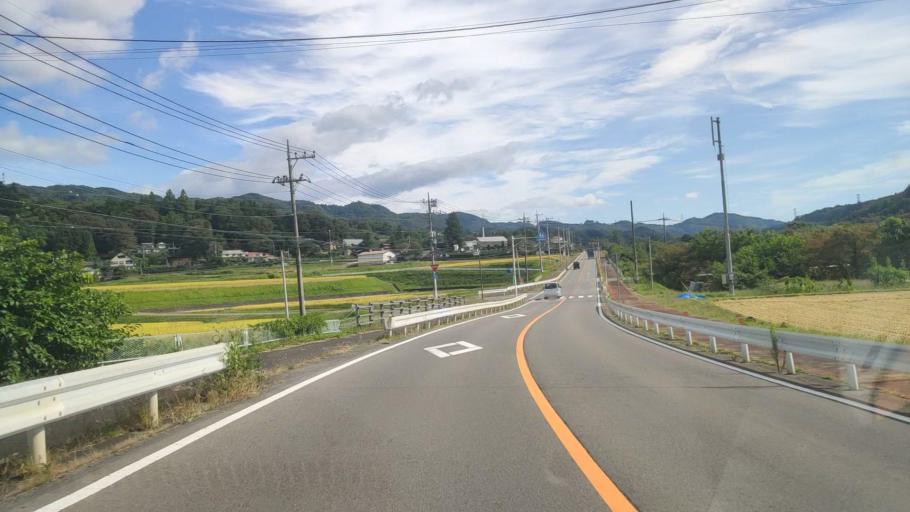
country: JP
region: Gunma
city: Nakanojomachi
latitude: 36.6139
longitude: 138.8874
